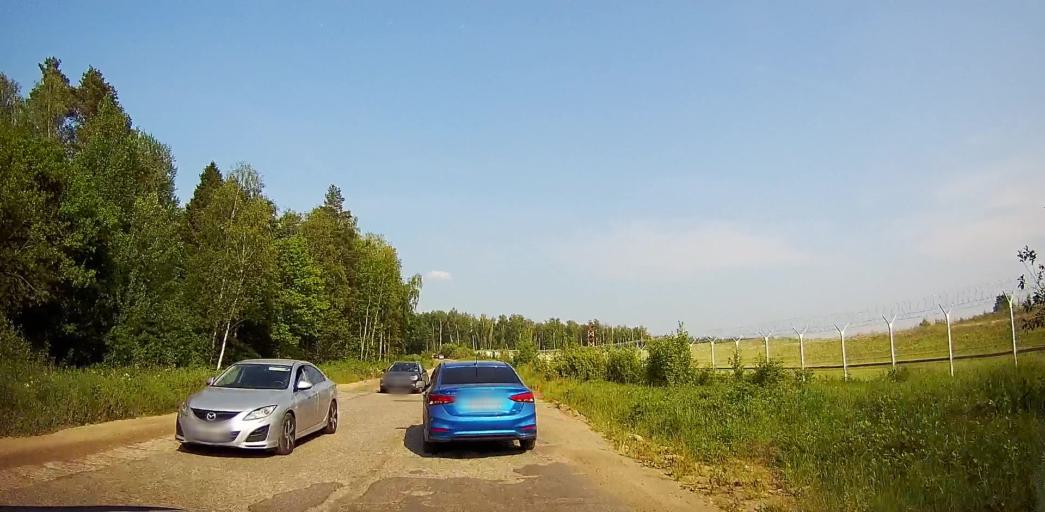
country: RU
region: Moskovskaya
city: Yakovlevskoye
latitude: 55.4311
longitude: 37.9066
